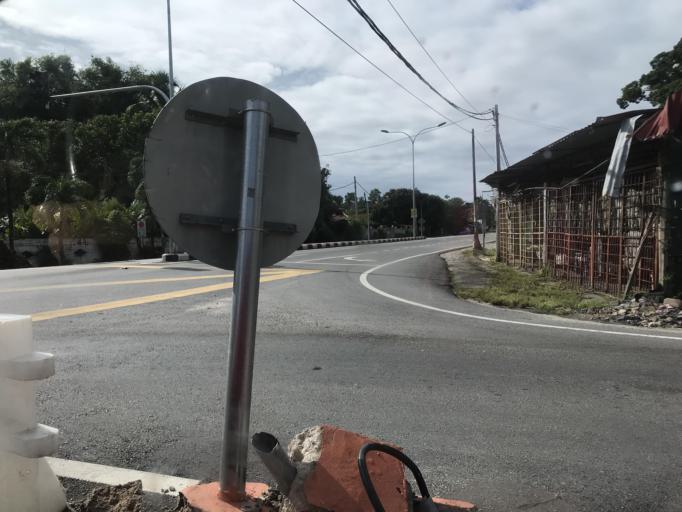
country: MY
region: Kelantan
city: Kota Bharu
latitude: 6.1317
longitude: 102.1767
